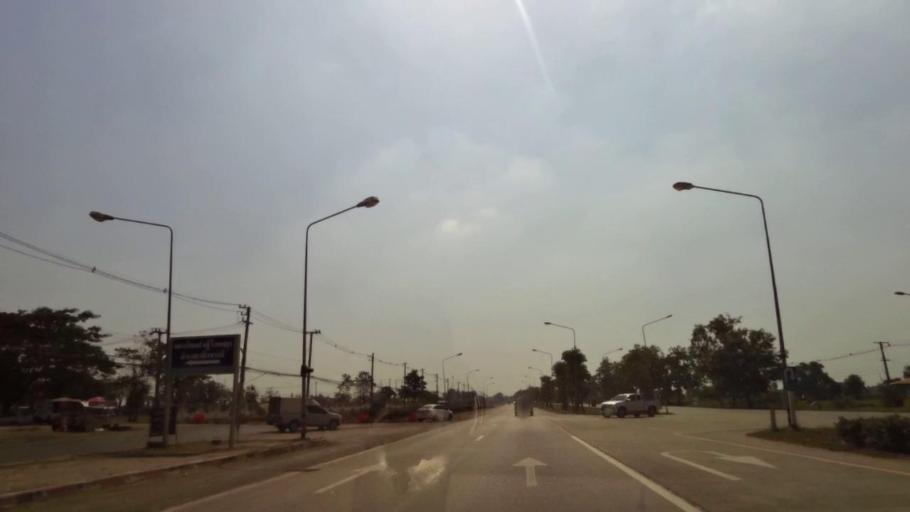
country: TH
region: Phichit
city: Wachira Barami
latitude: 16.5246
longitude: 100.1431
